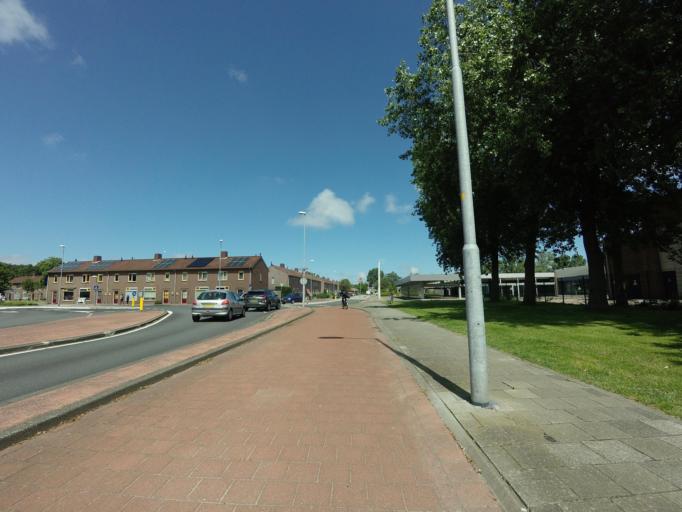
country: NL
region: North Holland
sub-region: Gemeente Den Helder
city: Den Helder
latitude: 52.9484
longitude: 4.7672
